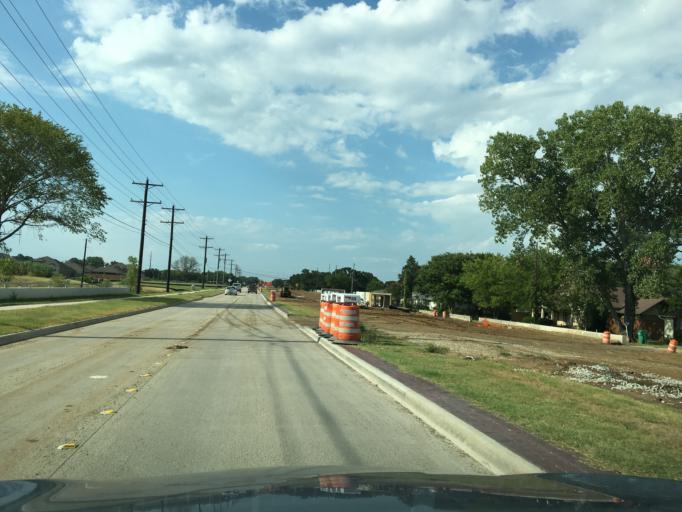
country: US
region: Texas
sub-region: Denton County
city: Denton
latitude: 33.2236
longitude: -97.0834
